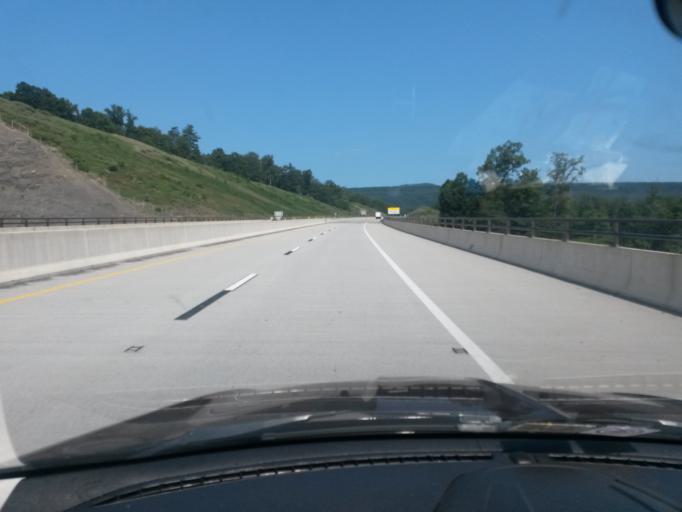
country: US
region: West Virginia
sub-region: Hardy County
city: Moorefield
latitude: 39.0823
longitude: -78.9719
